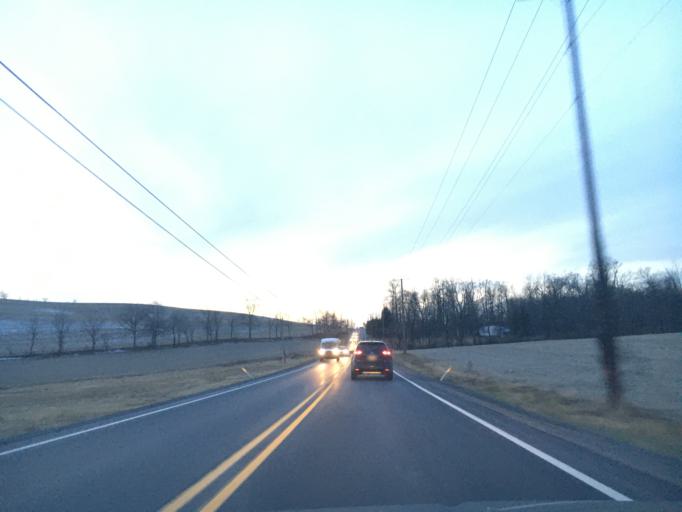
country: US
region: Pennsylvania
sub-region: Northampton County
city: Youngsville
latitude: 40.7525
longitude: -75.4855
